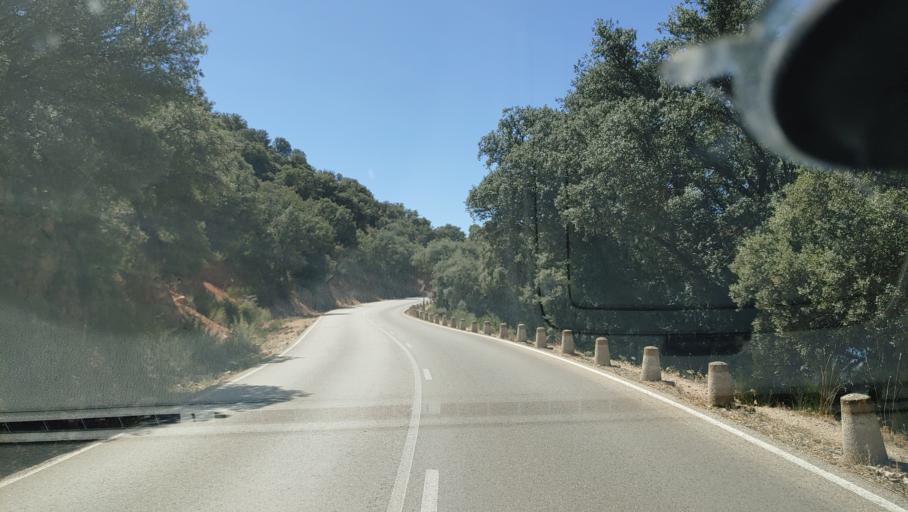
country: ES
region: Castille-La Mancha
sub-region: Provincia de Ciudad Real
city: Ruidera
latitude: 38.9596
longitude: -2.8609
